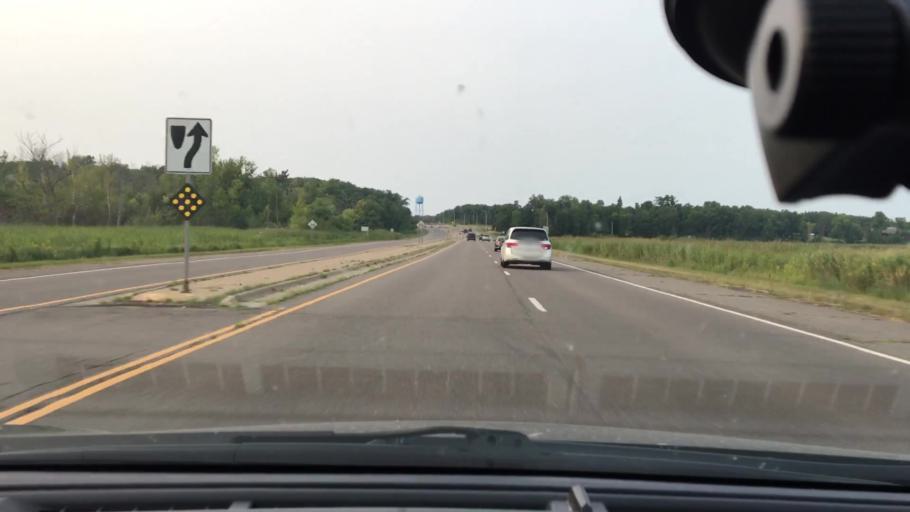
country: US
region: Minnesota
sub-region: Mille Lacs County
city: Vineland
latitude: 46.1719
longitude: -93.7581
